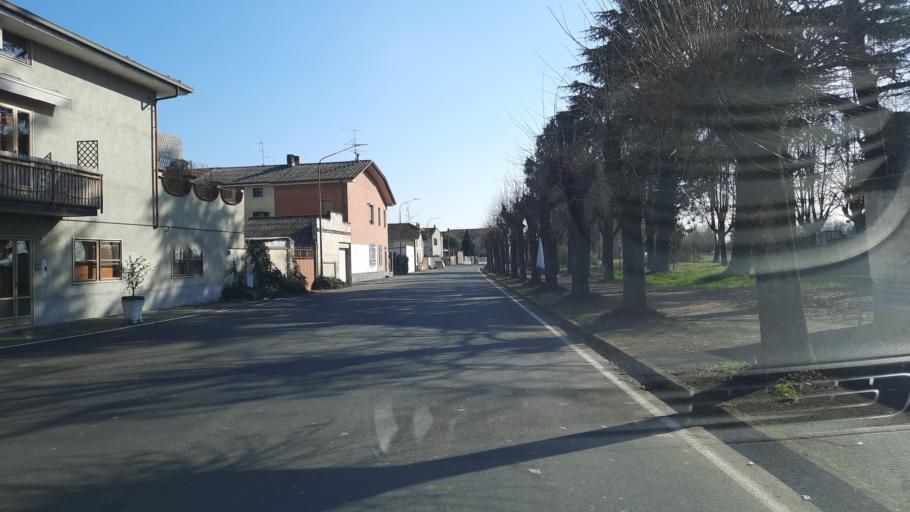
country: IT
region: Piedmont
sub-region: Provincia di Vercelli
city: Costanzana
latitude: 45.2349
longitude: 8.3701
